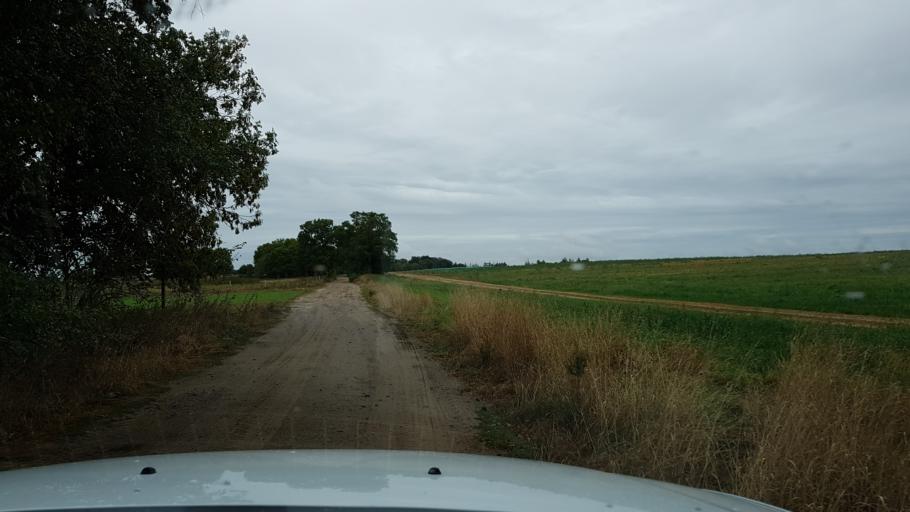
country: PL
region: West Pomeranian Voivodeship
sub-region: Powiat gryfinski
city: Moryn
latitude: 52.8419
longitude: 14.3001
